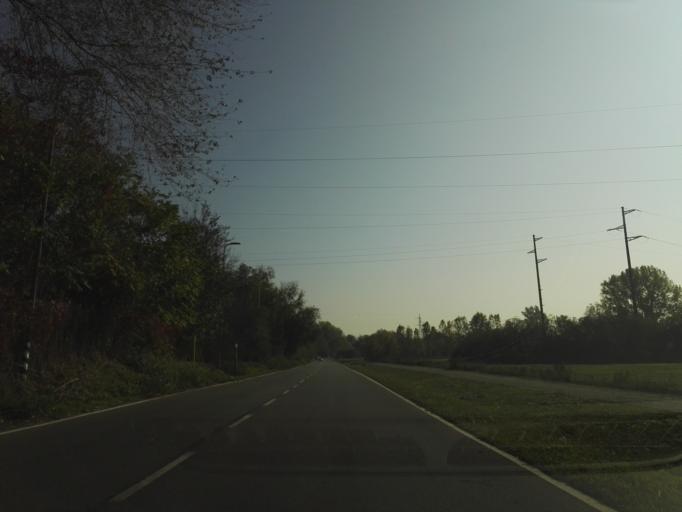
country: IT
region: Lombardy
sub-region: Citta metropolitana di Milano
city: Chiaravalle
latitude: 45.4222
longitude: 9.2353
